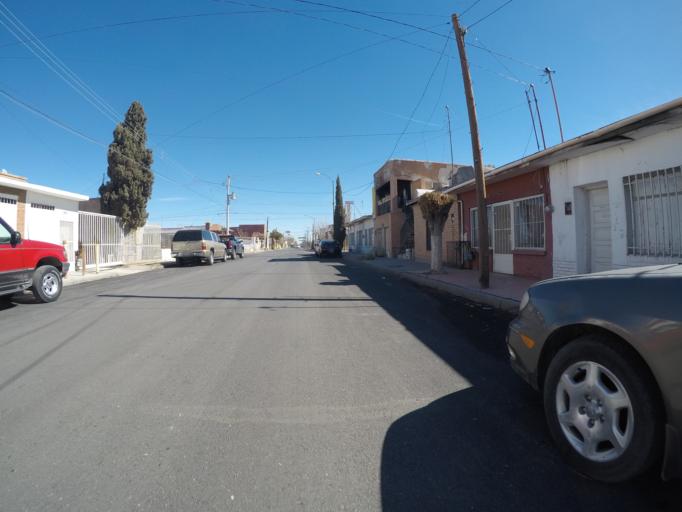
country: MX
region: Chihuahua
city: Ciudad Juarez
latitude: 31.7406
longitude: -106.4672
